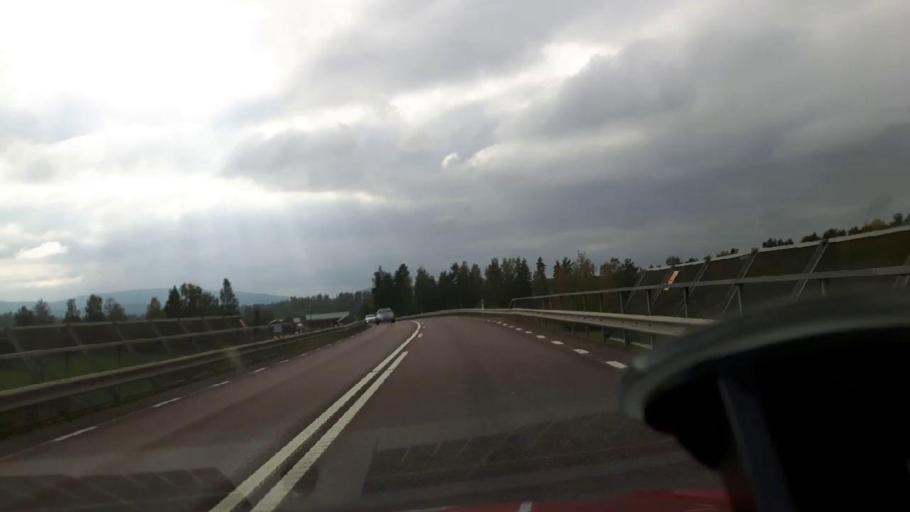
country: SE
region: Gaevleborg
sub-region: Bollnas Kommun
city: Kilafors
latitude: 61.2478
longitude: 16.5503
